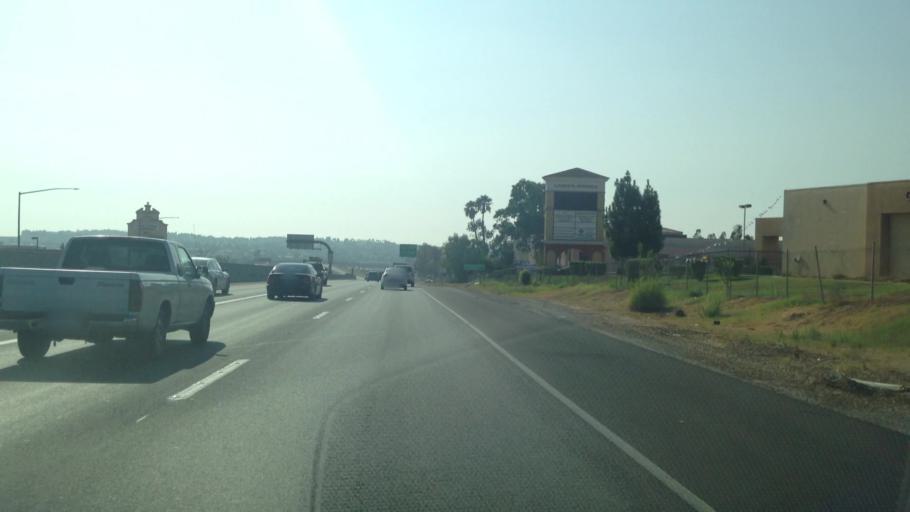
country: US
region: California
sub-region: Riverside County
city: Moreno Valley
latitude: 33.9435
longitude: -117.2833
